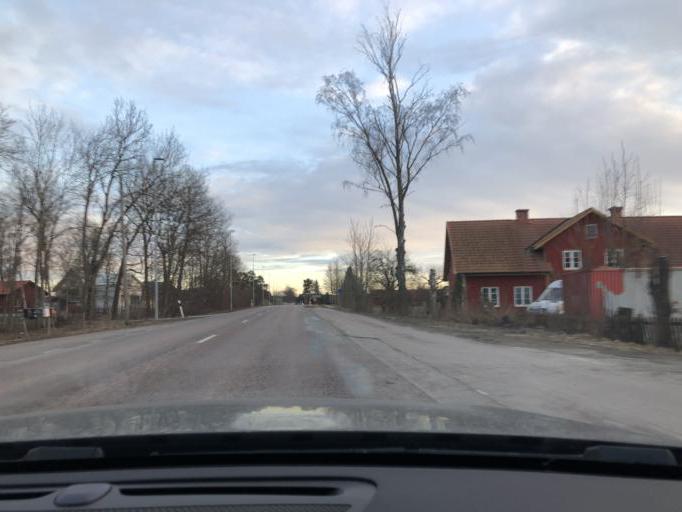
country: SE
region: Uppsala
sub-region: Uppsala Kommun
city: Gamla Uppsala
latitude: 59.9135
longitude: 17.6430
